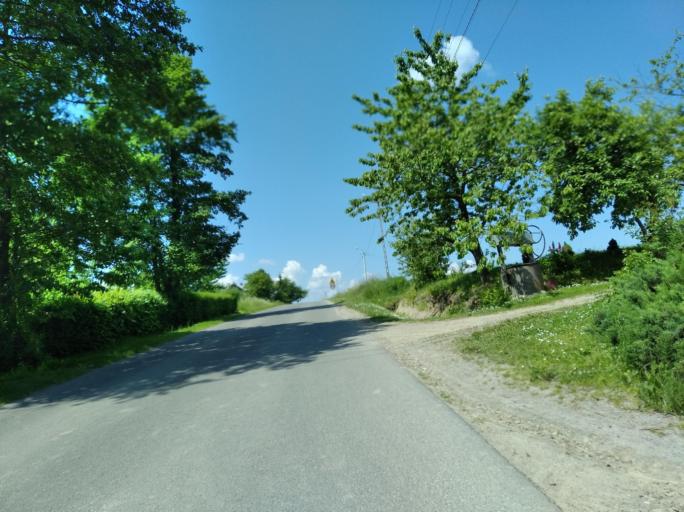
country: PL
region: Subcarpathian Voivodeship
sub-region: Powiat ropczycko-sedziszowski
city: Wielopole Skrzynskie
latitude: 49.9789
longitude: 21.6289
